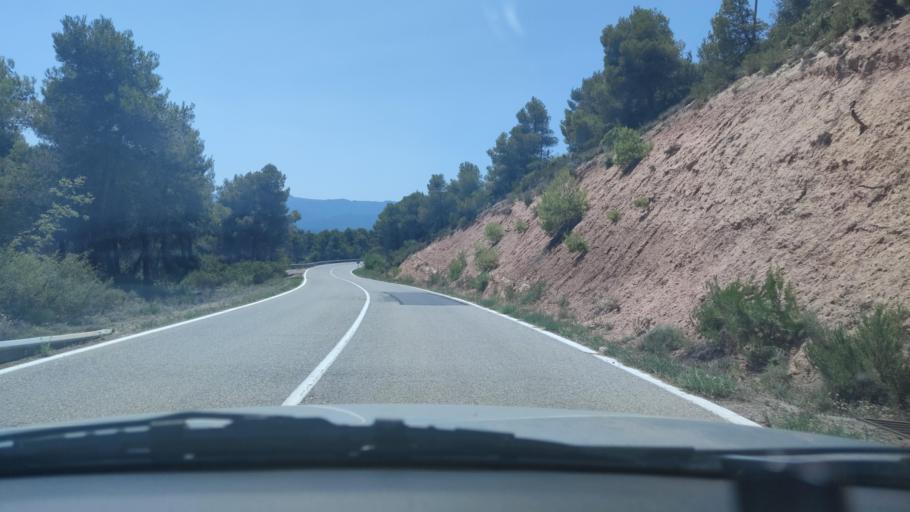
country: ES
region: Catalonia
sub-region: Provincia de Lleida
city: Fulleda
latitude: 41.4302
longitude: 1.0306
